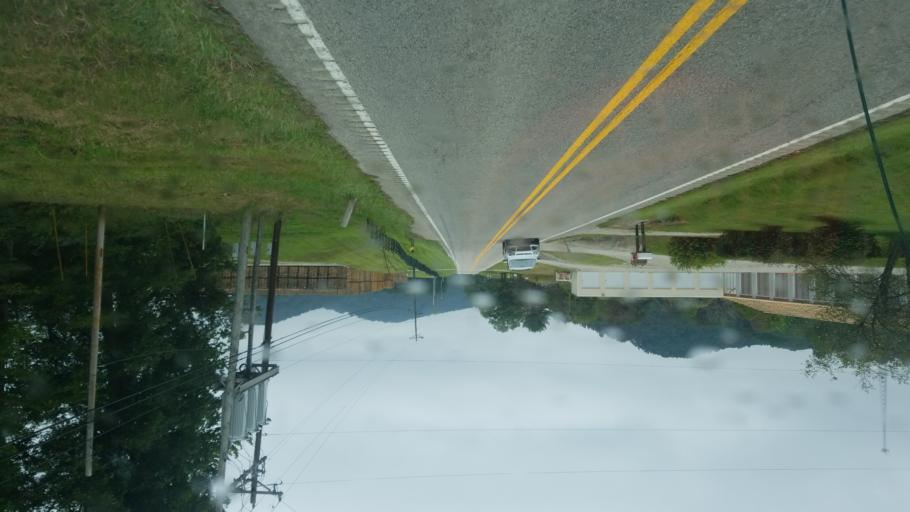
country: US
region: Kentucky
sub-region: Rowan County
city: Morehead
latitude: 38.2549
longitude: -83.4379
